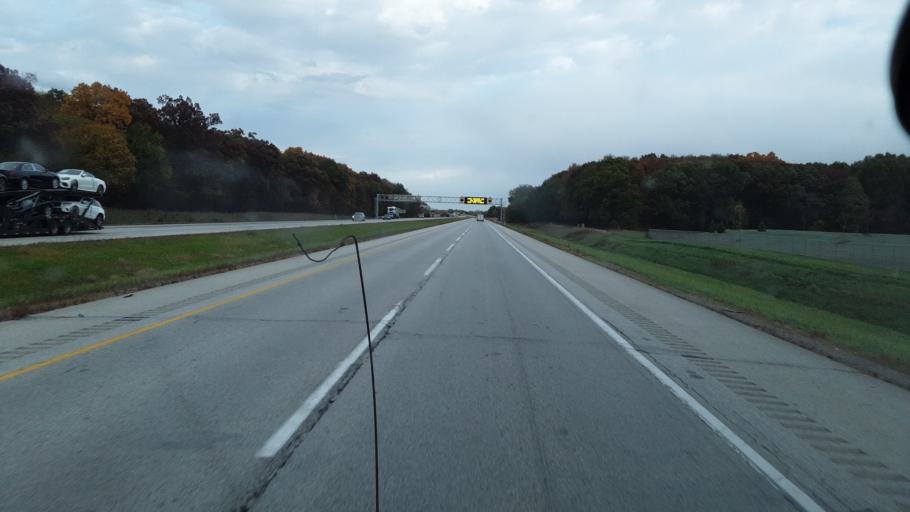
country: US
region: Indiana
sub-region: Elkhart County
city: Bristol
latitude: 41.7310
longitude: -85.8642
